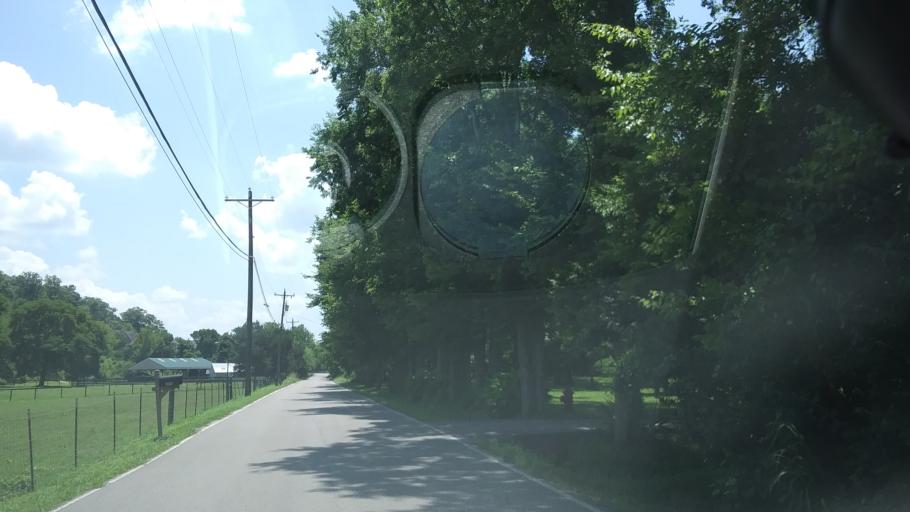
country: US
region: Tennessee
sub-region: Davidson County
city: Belle Meade
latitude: 36.1244
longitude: -86.9322
